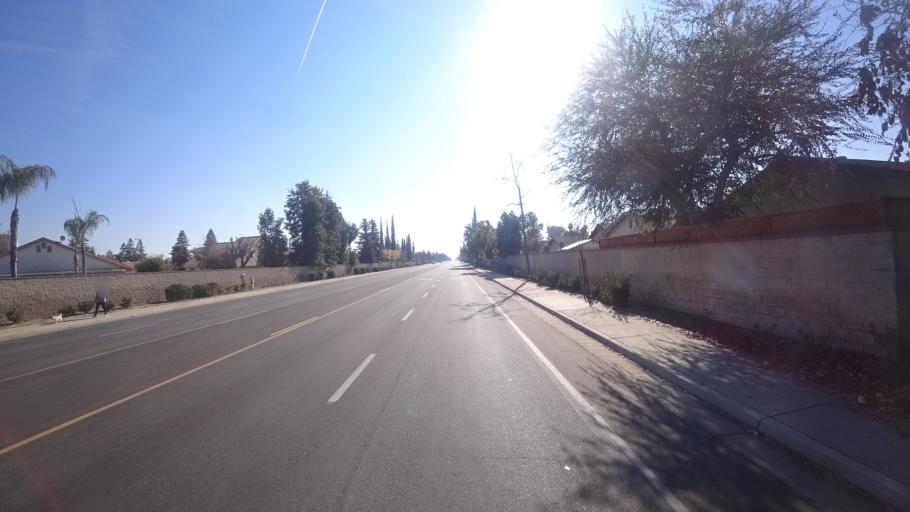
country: US
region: California
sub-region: Kern County
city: Greenacres
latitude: 35.3228
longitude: -119.1188
